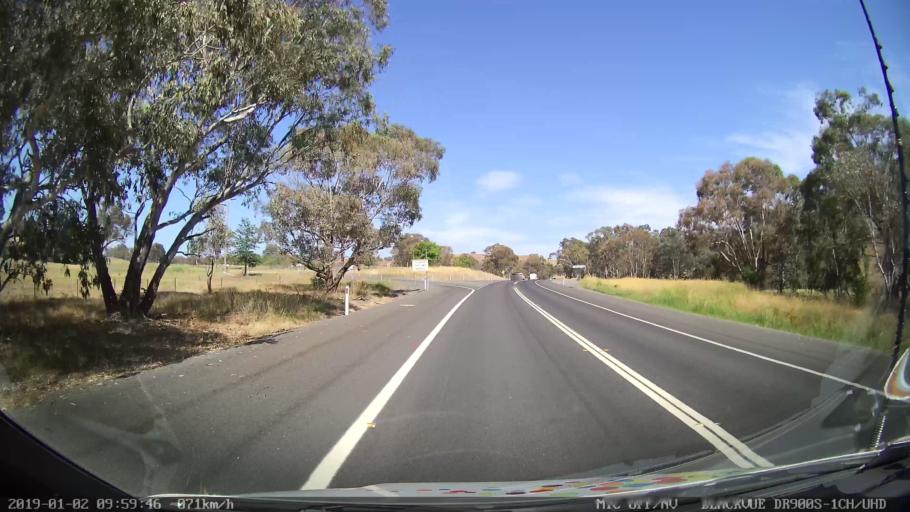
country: AU
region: New South Wales
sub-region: Tumut Shire
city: Tumut
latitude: -35.1978
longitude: 148.1391
